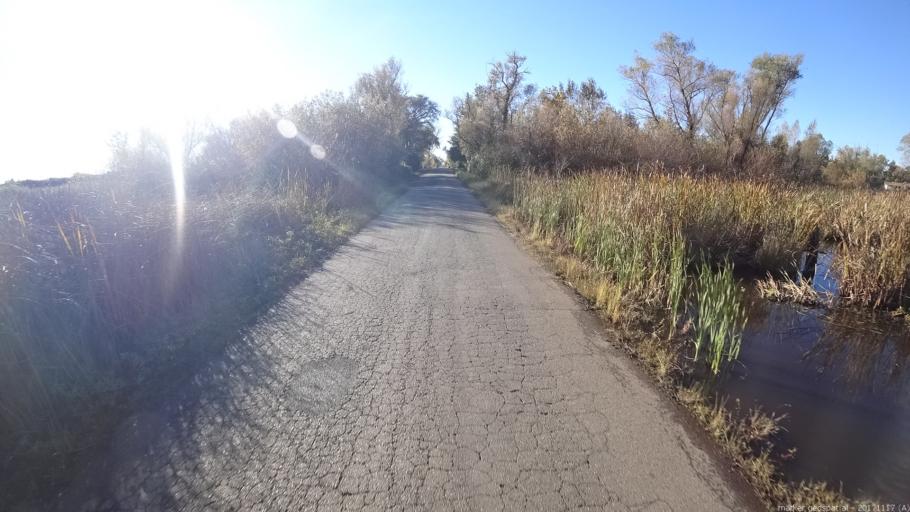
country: US
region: California
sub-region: Shasta County
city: Cottonwood
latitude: 40.4031
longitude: -122.2243
